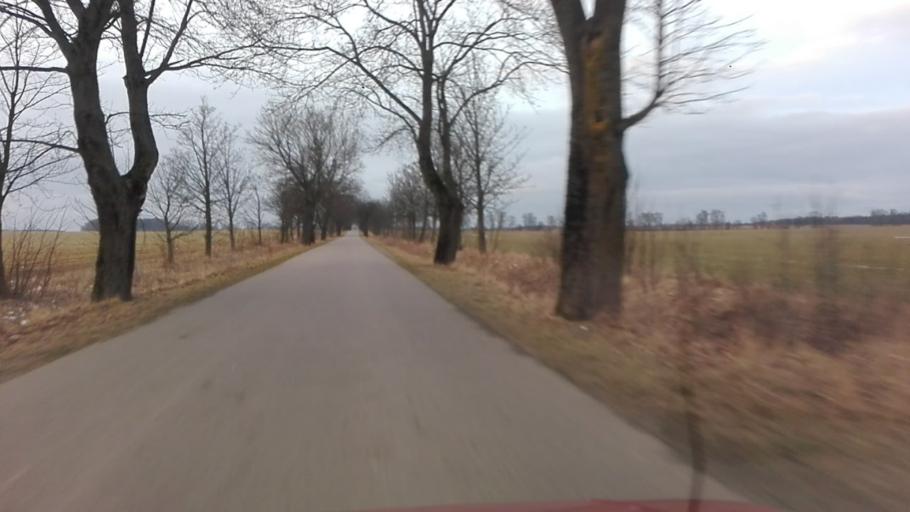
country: PL
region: West Pomeranian Voivodeship
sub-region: Powiat swidwinski
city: Rabino
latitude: 53.8089
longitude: 15.9173
